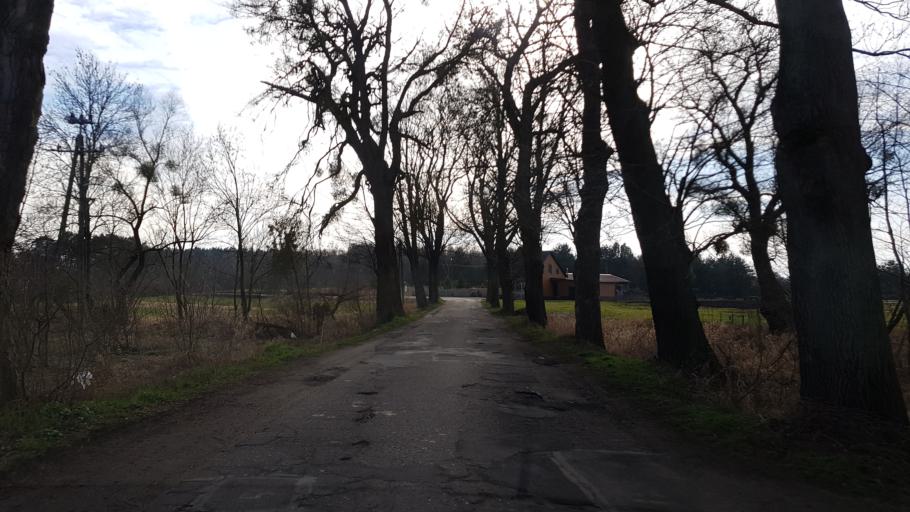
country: PL
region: West Pomeranian Voivodeship
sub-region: Powiat policki
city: Dobra
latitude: 53.5165
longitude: 14.3499
